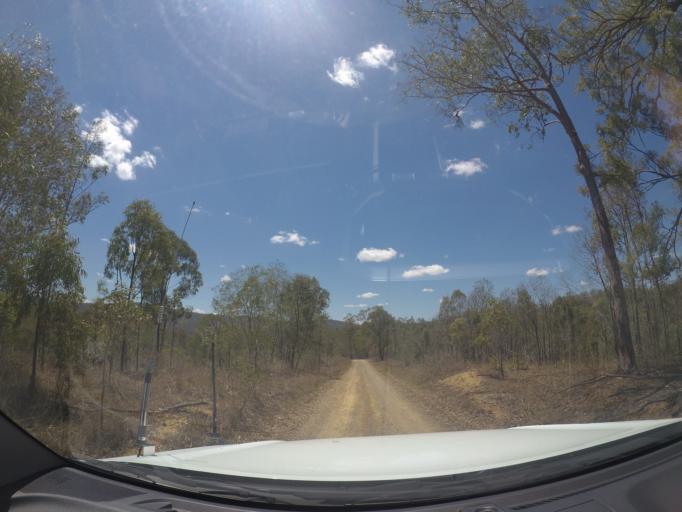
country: AU
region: Queensland
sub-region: Ipswich
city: Springfield Lakes
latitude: -27.8236
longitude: 152.8408
